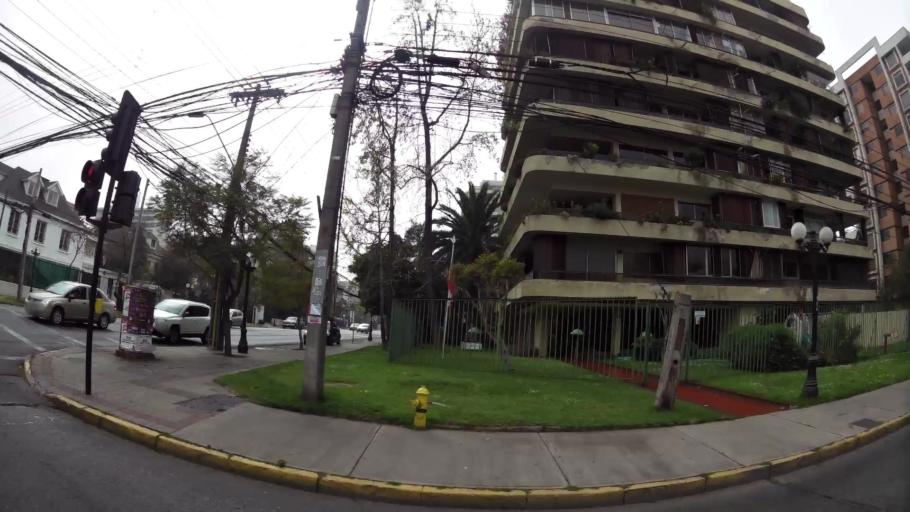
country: CL
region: Santiago Metropolitan
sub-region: Provincia de Santiago
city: Villa Presidente Frei, Nunoa, Santiago, Chile
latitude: -33.4297
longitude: -70.6007
